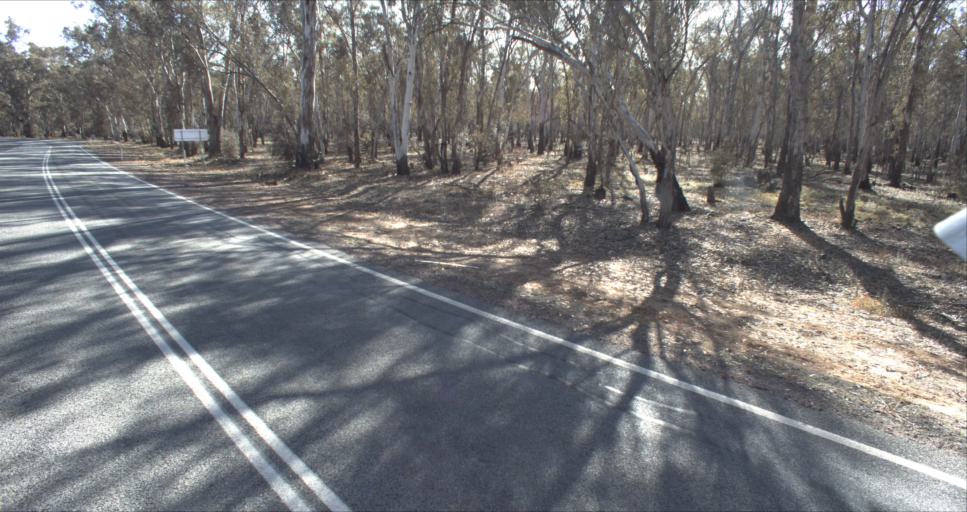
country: AU
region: New South Wales
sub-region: Leeton
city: Leeton
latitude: -34.6306
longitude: 146.3758
